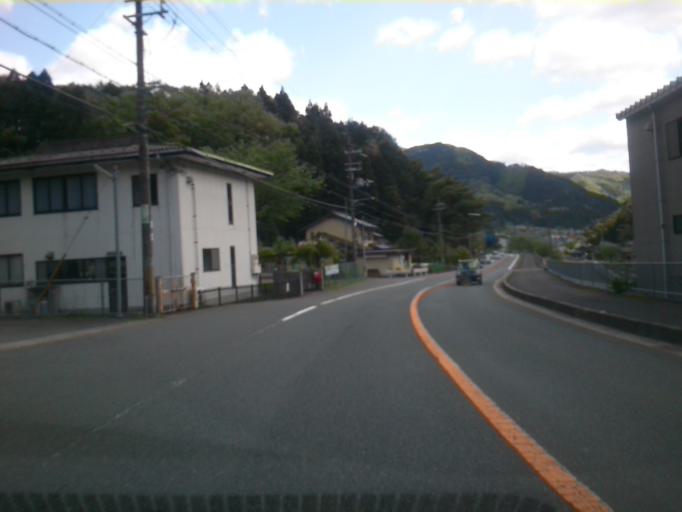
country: JP
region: Kyoto
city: Fukuchiyama
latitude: 35.3375
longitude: 135.0696
